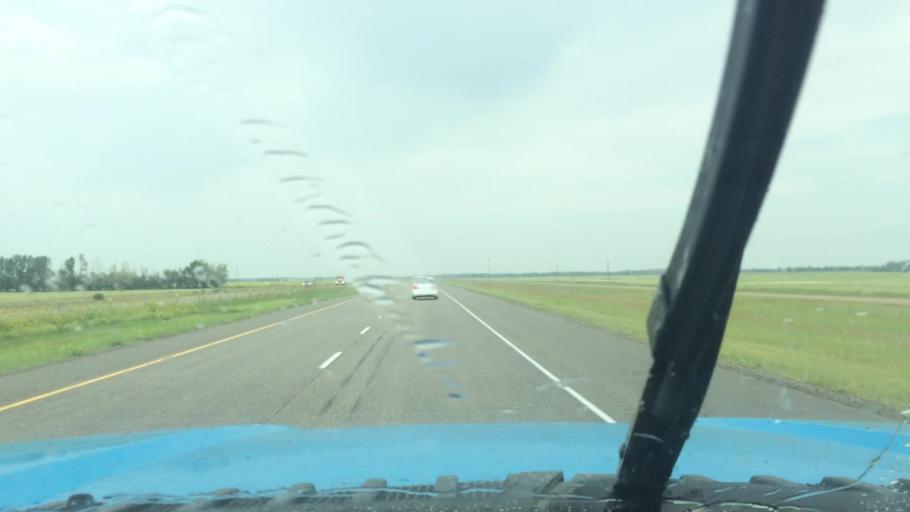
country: CA
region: Alberta
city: Olds
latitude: 51.7249
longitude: -114.0253
